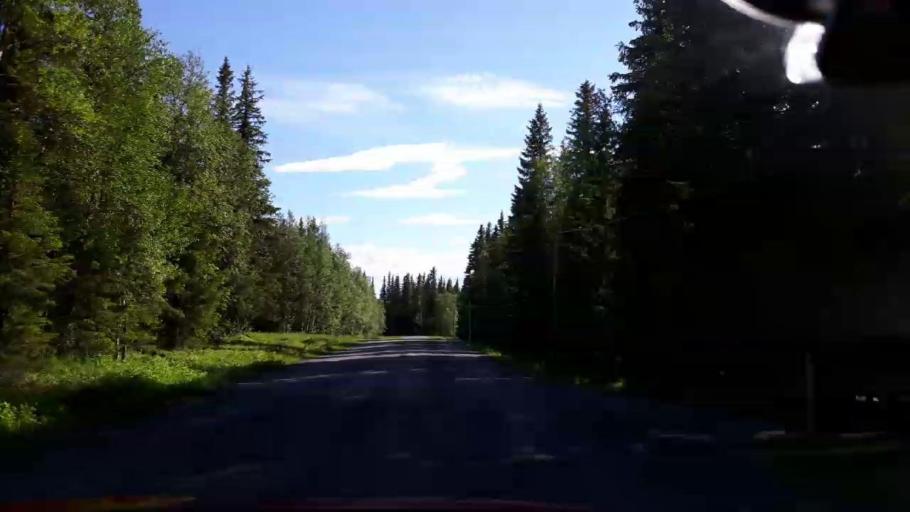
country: SE
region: Jaemtland
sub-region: Krokoms Kommun
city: Valla
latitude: 63.7353
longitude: 14.1188
